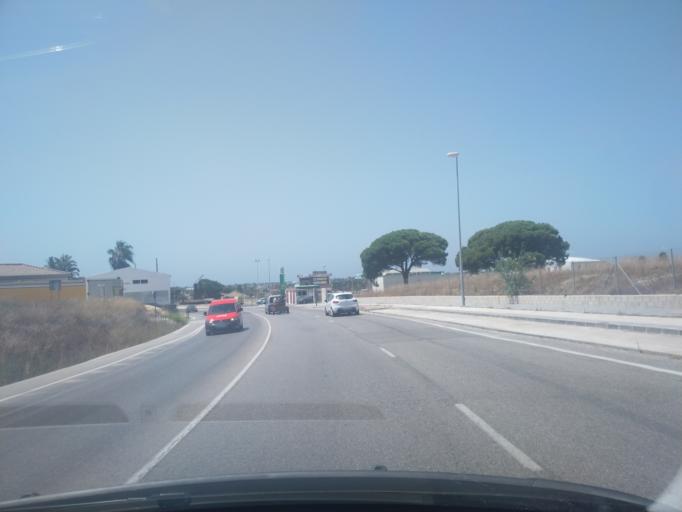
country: ES
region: Andalusia
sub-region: Provincia de Cadiz
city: Chiclana de la Frontera
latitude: 36.3938
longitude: -6.1452
